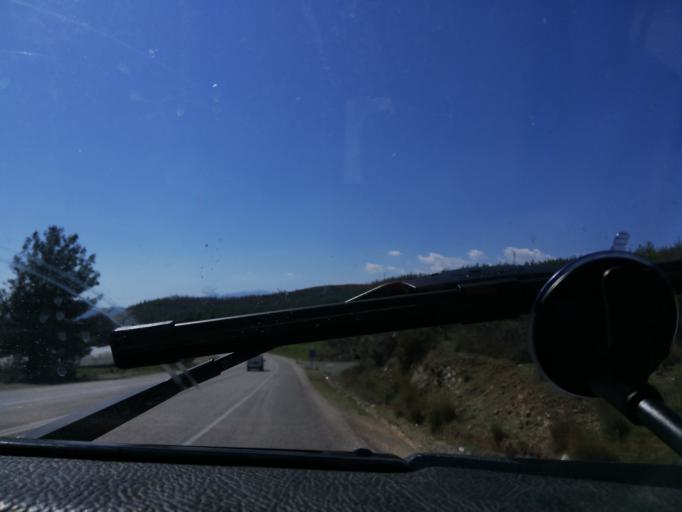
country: TR
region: Mugla
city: Kemer
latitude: 36.6078
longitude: 29.3572
